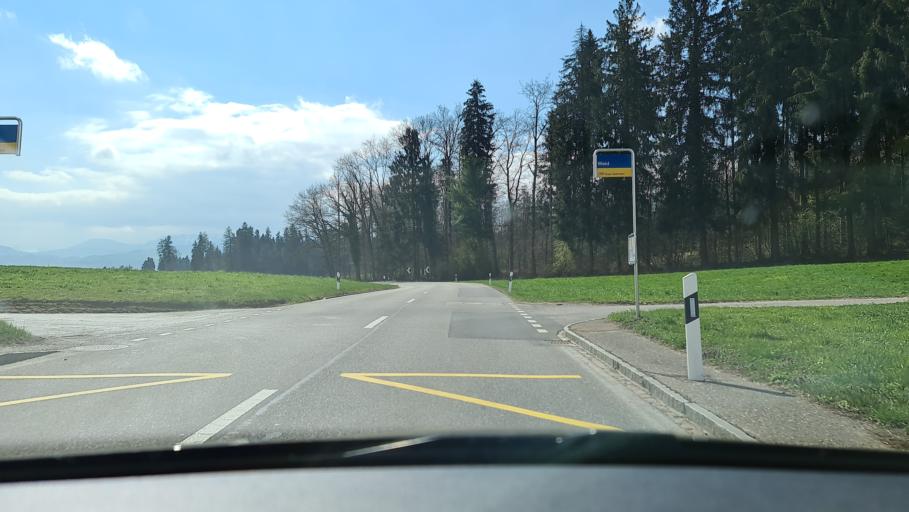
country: CH
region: Zug
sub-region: Zug
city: Steinhausen
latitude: 47.2174
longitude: 8.5027
